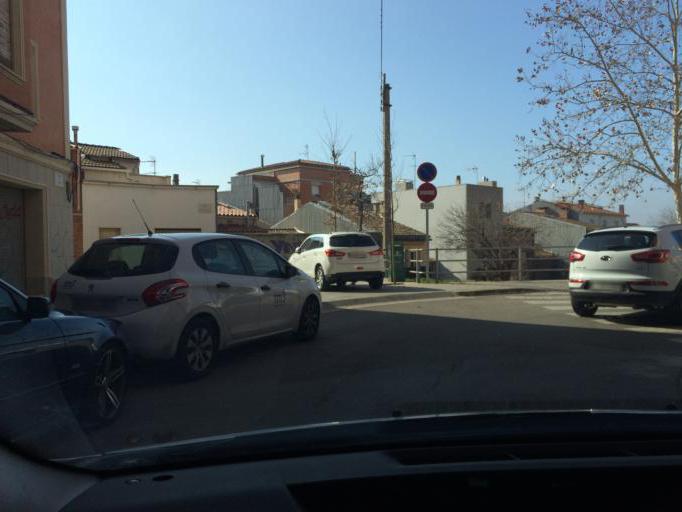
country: ES
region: Catalonia
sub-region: Provincia de Barcelona
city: Manresa
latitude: 41.7275
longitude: 1.8187
